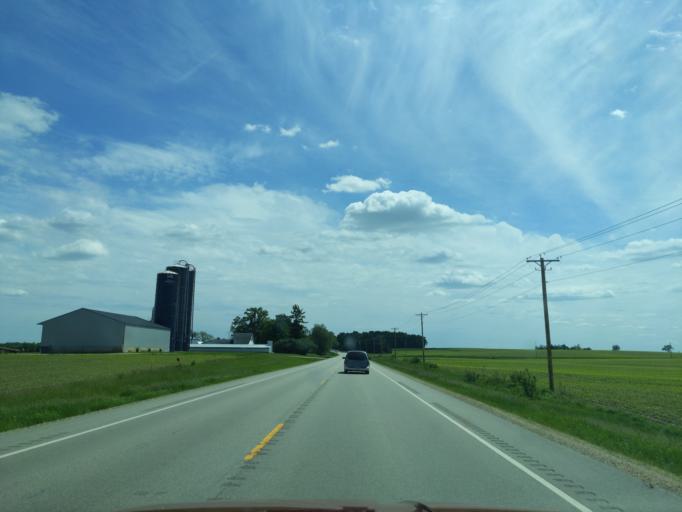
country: US
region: Wisconsin
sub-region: Columbia County
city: Poynette
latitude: 43.3572
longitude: -89.3285
